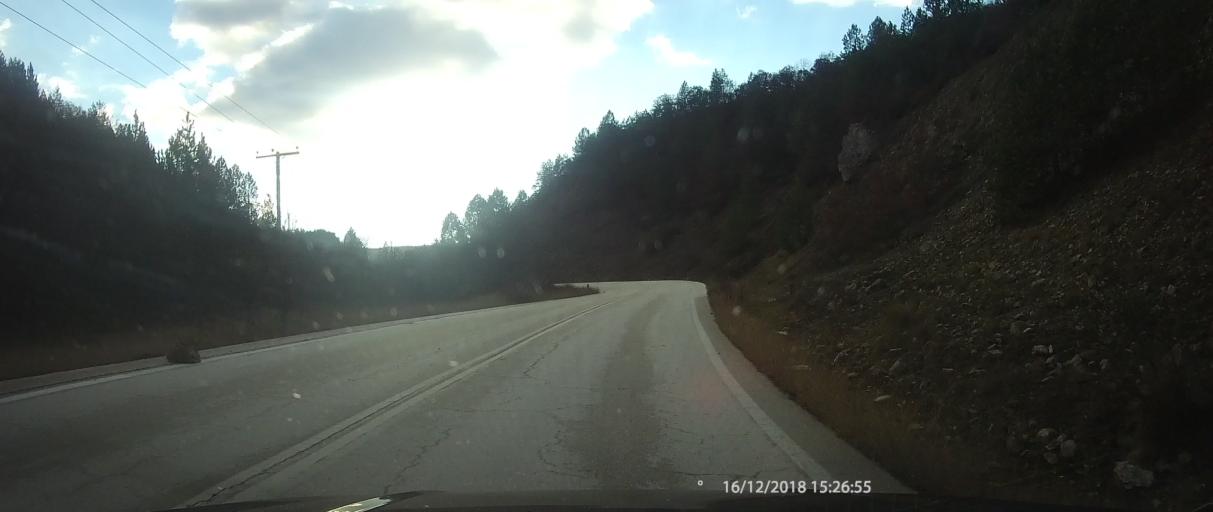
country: GR
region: Epirus
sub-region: Nomos Ioanninon
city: Konitsa
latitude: 40.1125
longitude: 20.7756
